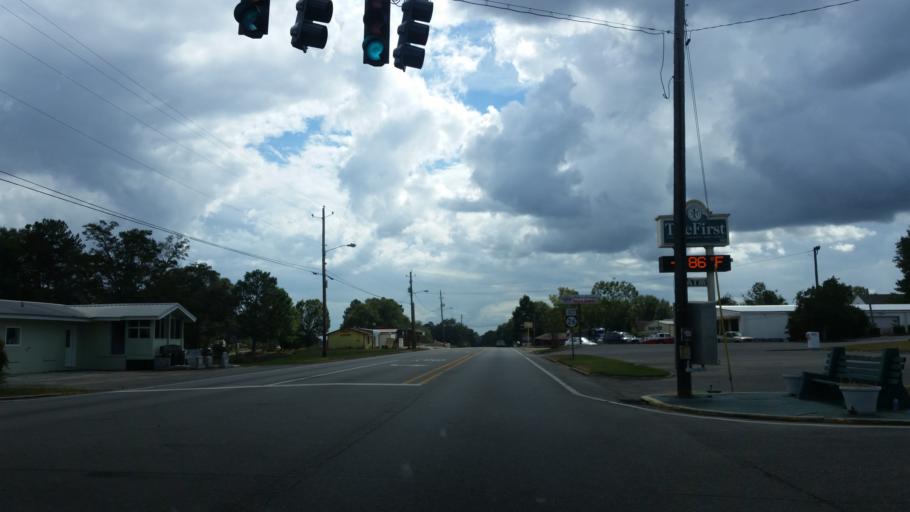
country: US
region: Mississippi
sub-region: Stone County
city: Wiggins
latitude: 30.8554
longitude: -89.1385
